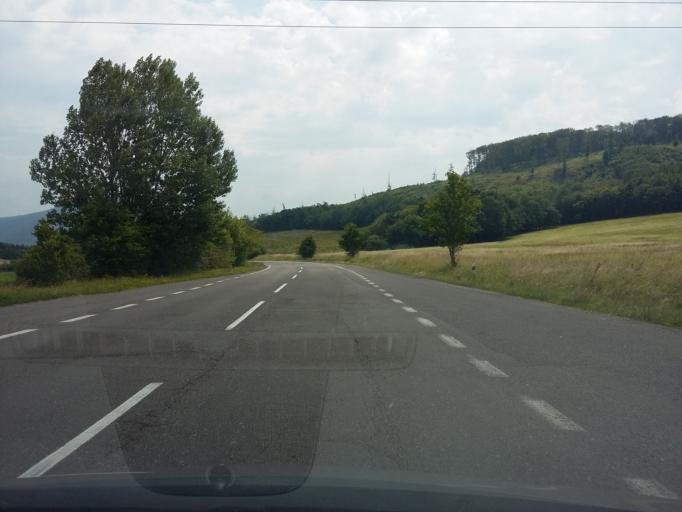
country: SK
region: Bratislavsky
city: Modra
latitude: 48.4591
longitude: 17.2025
